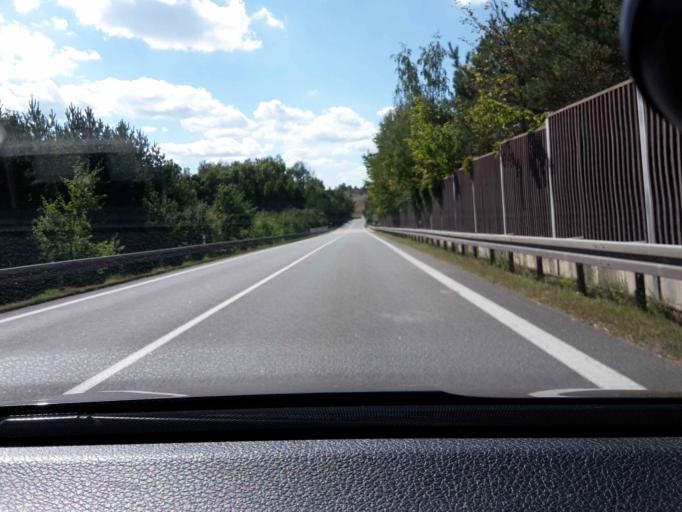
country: CZ
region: Jihocesky
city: Strmilov
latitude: 49.1605
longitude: 15.2081
